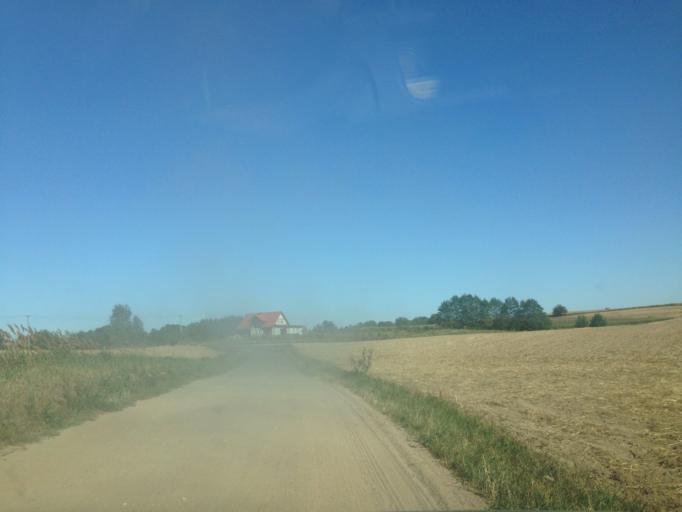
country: PL
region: Kujawsko-Pomorskie
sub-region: Powiat brodnicki
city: Brodnica
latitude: 53.2108
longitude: 19.4620
